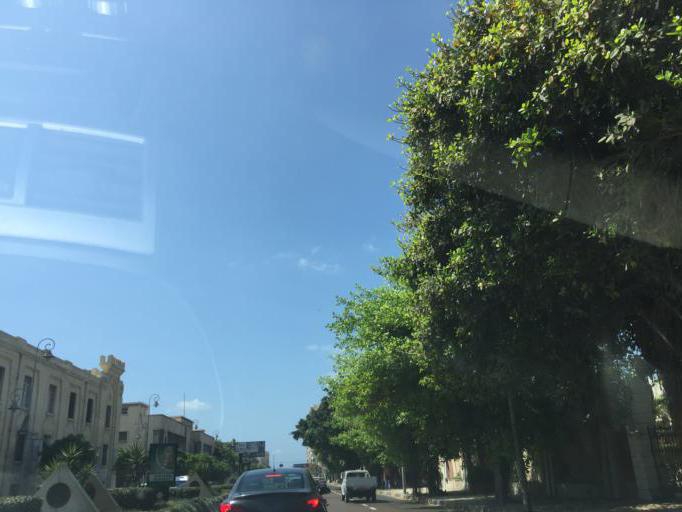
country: EG
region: Alexandria
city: Alexandria
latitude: 31.2054
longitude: 29.9144
